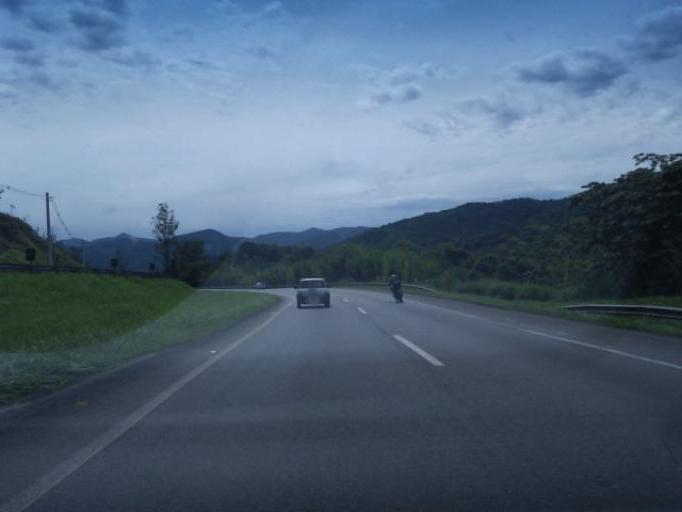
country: BR
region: Sao Paulo
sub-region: Miracatu
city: Miracatu
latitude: -24.1470
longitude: -47.3005
